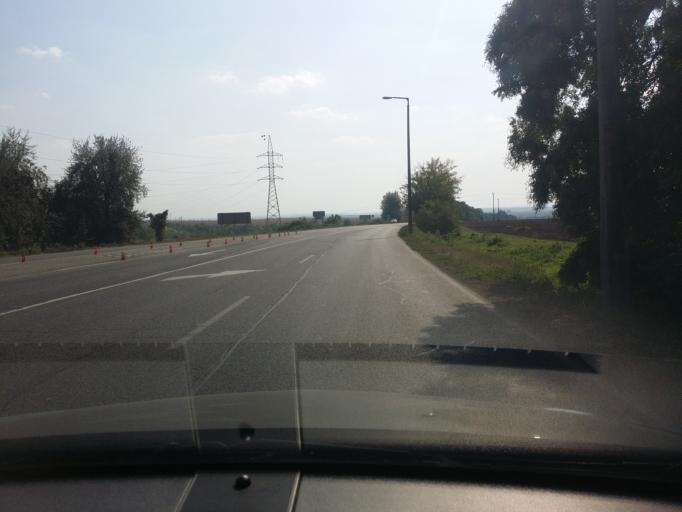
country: HU
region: Fejer
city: Dunaujvaros
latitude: 46.9247
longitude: 18.9306
